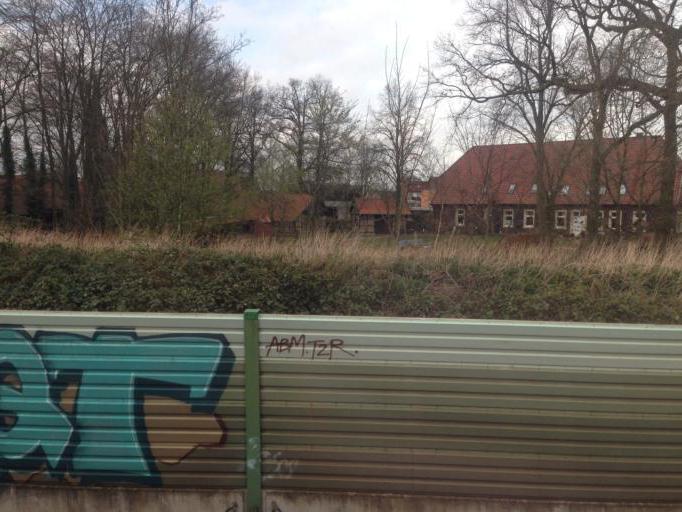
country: DE
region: North Rhine-Westphalia
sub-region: Regierungsbezirk Munster
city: Nottuln
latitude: 51.8635
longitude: 7.3724
